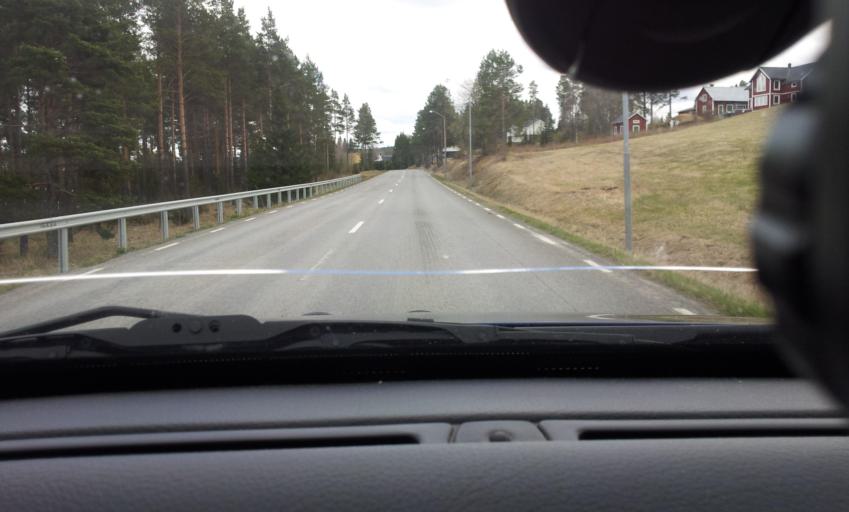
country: SE
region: Jaemtland
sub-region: OEstersunds Kommun
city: Ostersund
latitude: 63.1394
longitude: 14.6299
